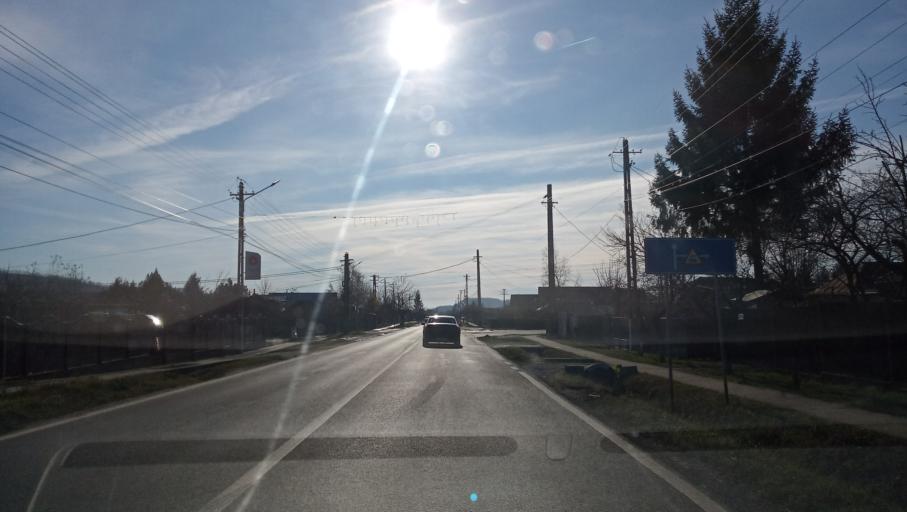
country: RO
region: Prahova
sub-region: Comuna Gura Vitioarei
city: Gura Vitioarei
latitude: 45.1621
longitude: 26.0307
